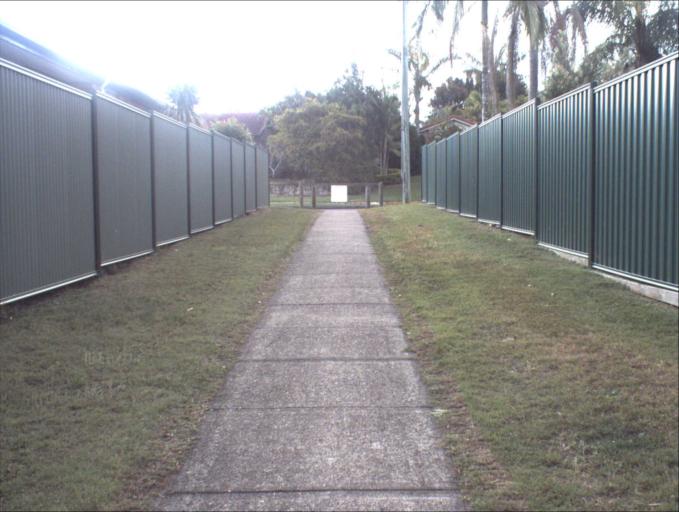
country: AU
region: Queensland
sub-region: Logan
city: Park Ridge South
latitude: -27.6792
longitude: 153.0393
